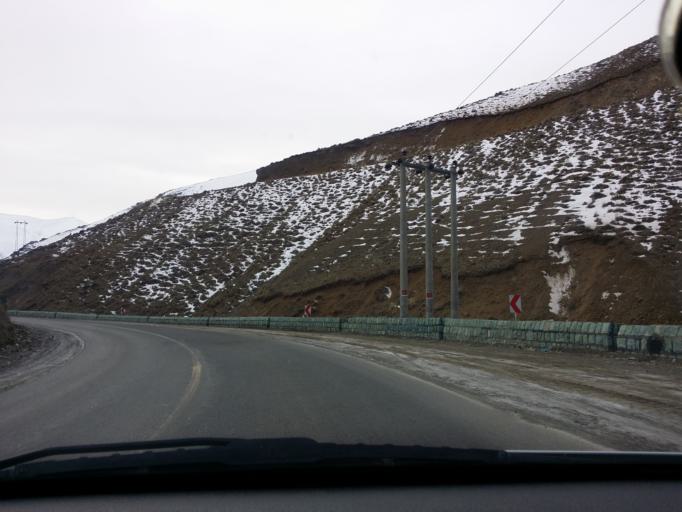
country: IR
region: Tehran
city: Tajrish
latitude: 36.1762
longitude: 51.3141
